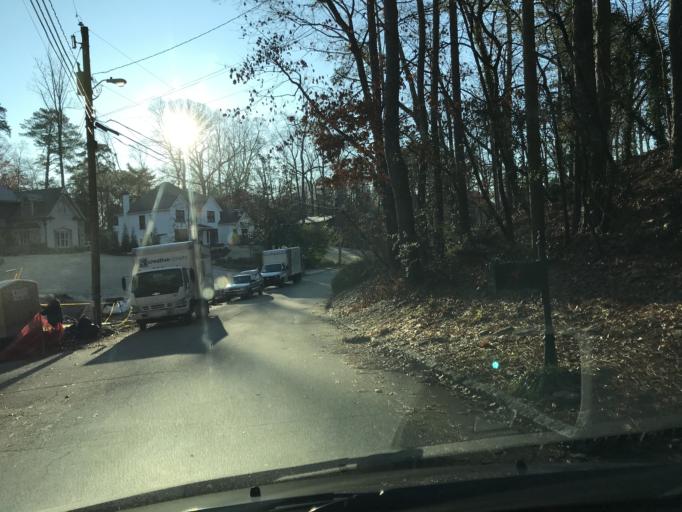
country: US
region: Georgia
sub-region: DeKalb County
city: North Atlanta
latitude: 33.8828
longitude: -84.3336
